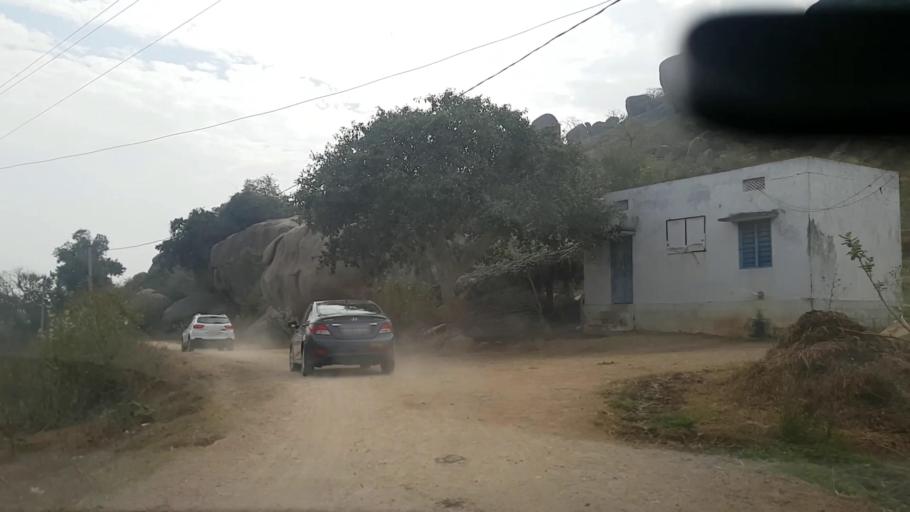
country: IN
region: Telangana
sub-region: Rangareddi
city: Lal Bahadur Nagar
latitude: 17.1801
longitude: 78.7827
